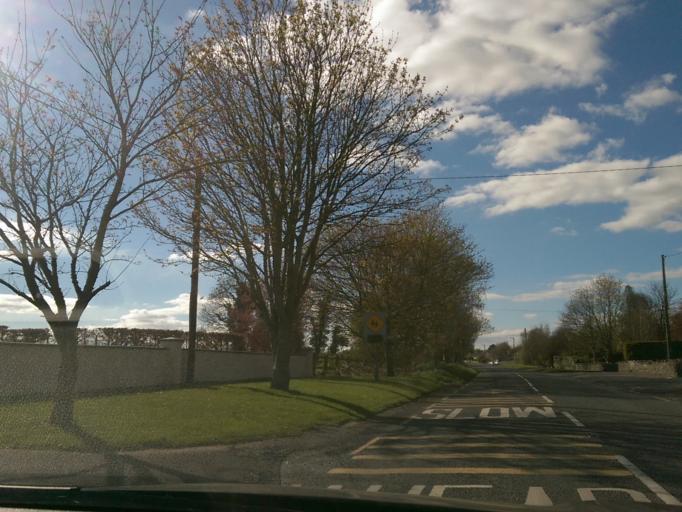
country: IE
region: Leinster
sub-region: Uibh Fhaili
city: Birr
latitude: 53.0881
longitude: -7.9356
